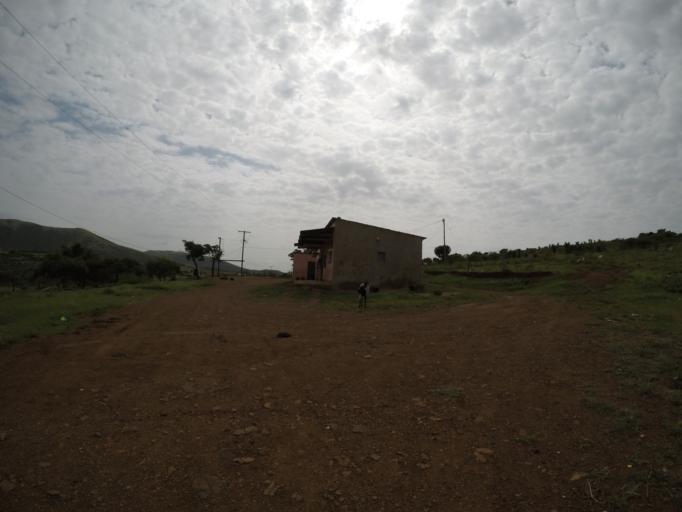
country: ZA
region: KwaZulu-Natal
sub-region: uThungulu District Municipality
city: Empangeni
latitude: -28.6237
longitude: 31.9006
